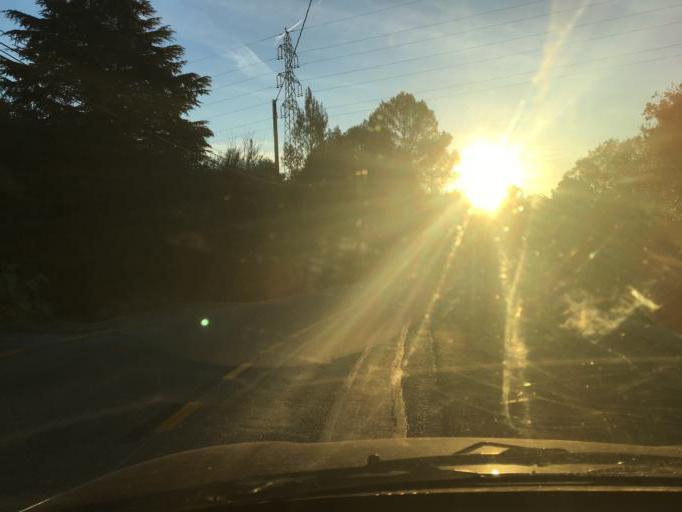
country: FR
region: Provence-Alpes-Cote d'Azur
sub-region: Departement du Var
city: Taradeau
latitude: 43.4599
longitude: 6.4181
